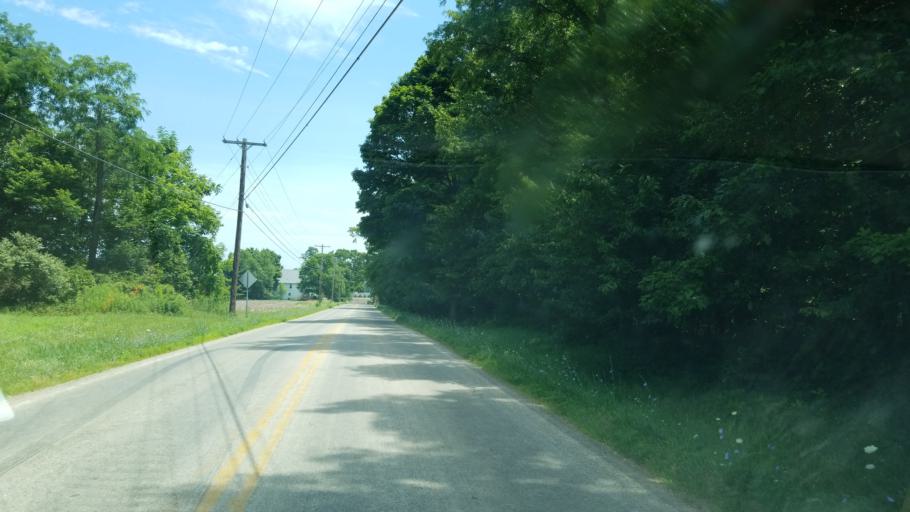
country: US
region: Ohio
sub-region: Ashland County
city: Ashland
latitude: 40.8656
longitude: -82.3484
